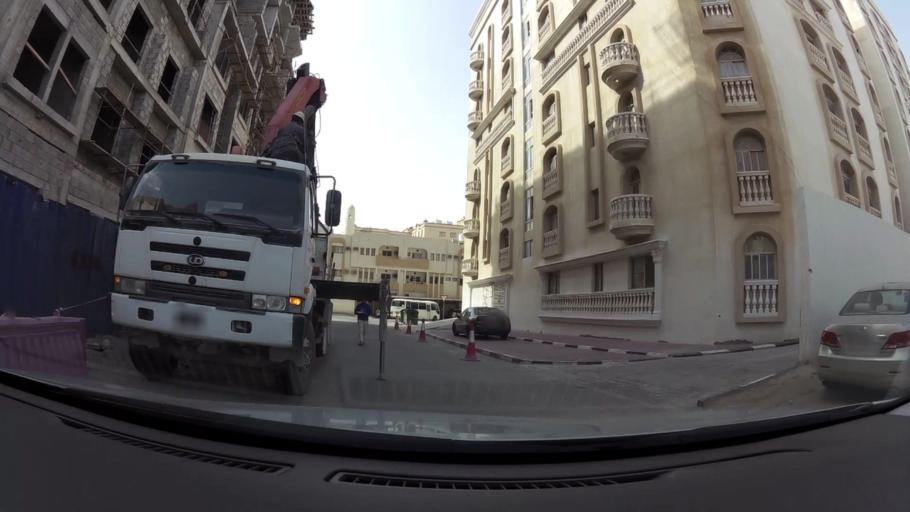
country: QA
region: Baladiyat ad Dawhah
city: Doha
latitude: 25.2876
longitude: 51.5079
